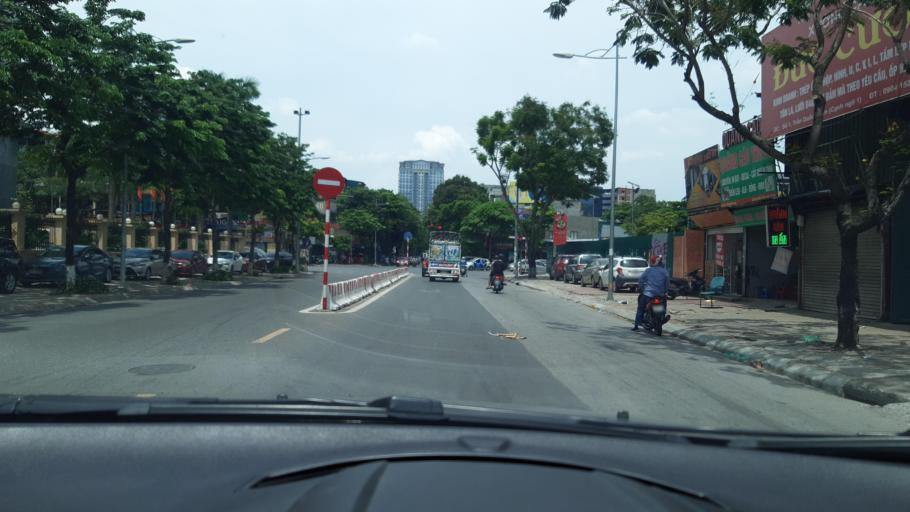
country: VN
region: Ha Noi
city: Cau Giay
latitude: 21.0416
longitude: 105.7895
